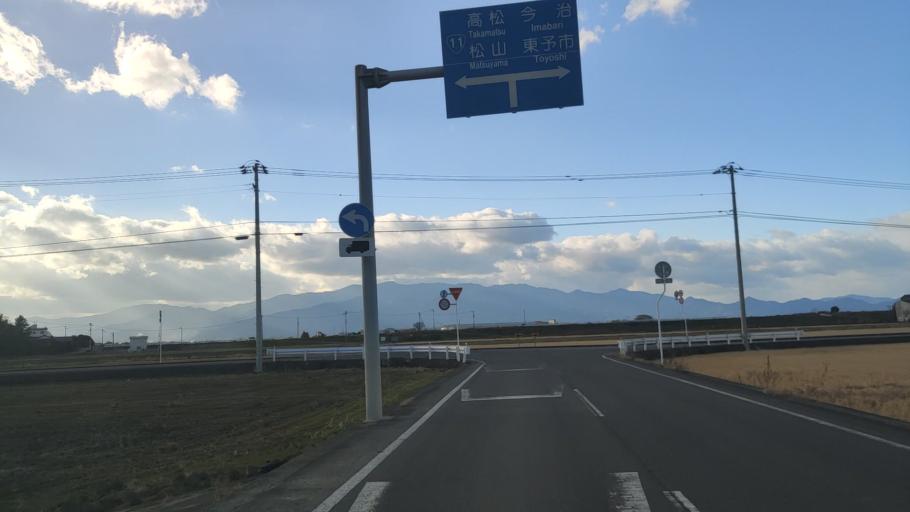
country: JP
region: Ehime
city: Saijo
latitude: 33.9043
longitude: 133.1297
